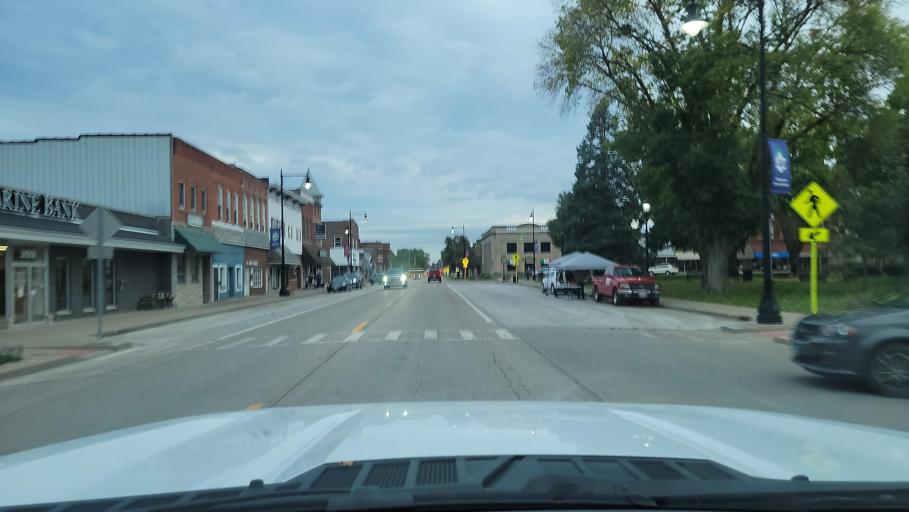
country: US
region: Illinois
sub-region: Schuyler County
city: Rushville
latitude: 40.1206
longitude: -90.5636
